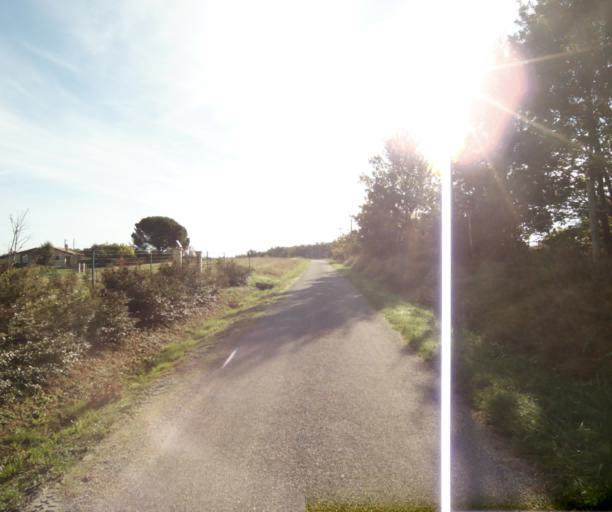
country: FR
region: Midi-Pyrenees
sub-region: Departement du Tarn-et-Garonne
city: Nohic
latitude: 43.9279
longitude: 1.4627
